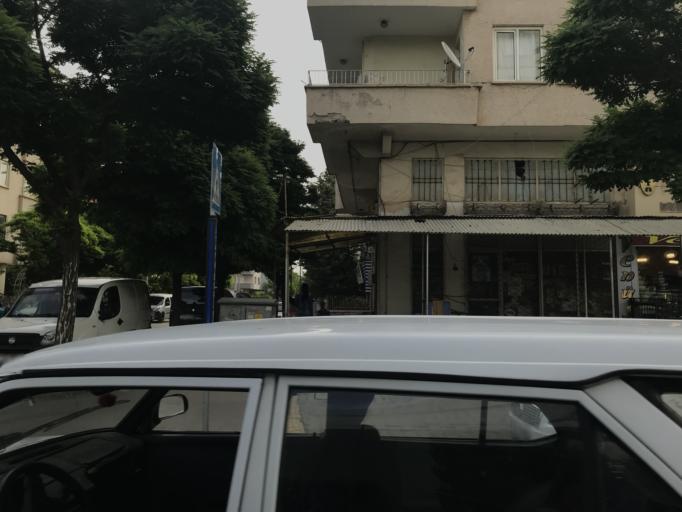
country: TR
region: Gaziantep
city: Sahinbey
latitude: 37.0534
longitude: 37.3343
